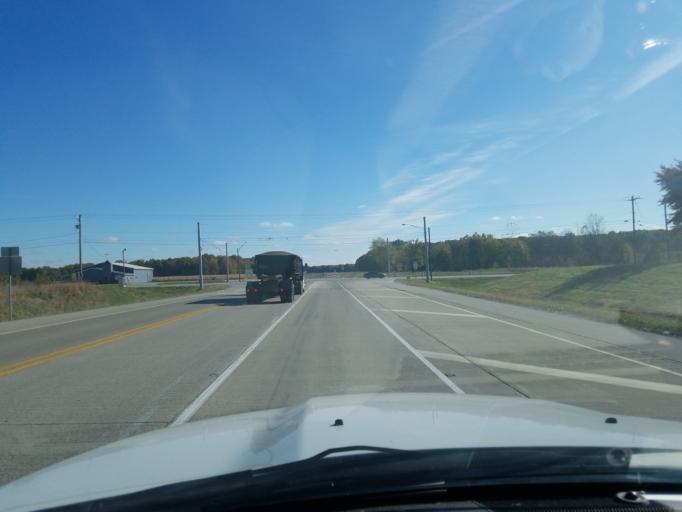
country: US
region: Indiana
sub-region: Jennings County
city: North Vernon
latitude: 39.0332
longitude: -85.6415
